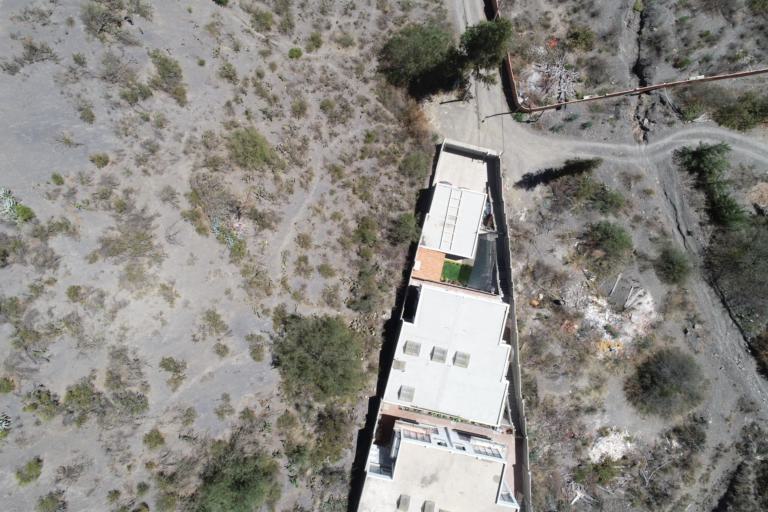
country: BO
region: La Paz
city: La Paz
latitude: -16.6280
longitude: -68.0501
